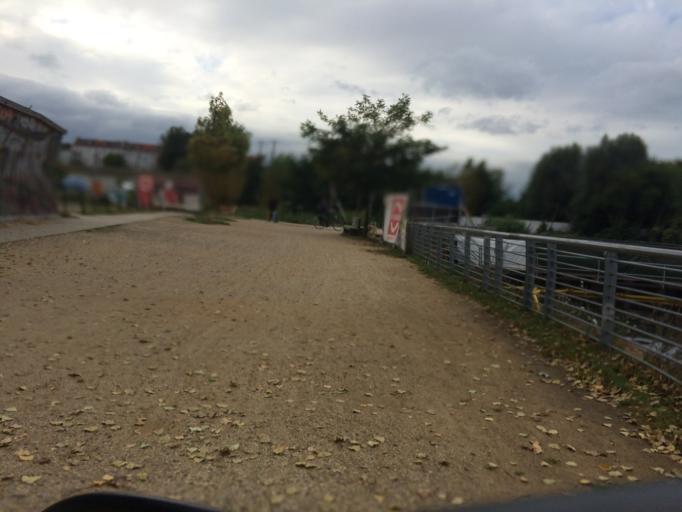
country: DE
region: Berlin
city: Treptow Bezirk
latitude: 52.4984
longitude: 13.4703
